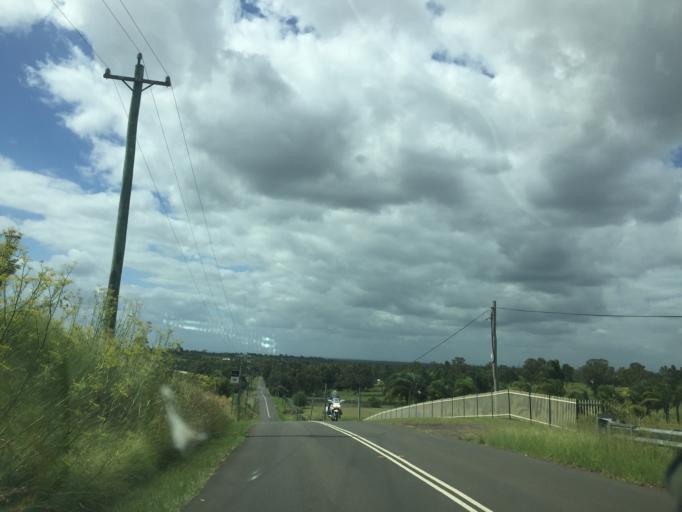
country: AU
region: New South Wales
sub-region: Penrith Municipality
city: Kingswood Park
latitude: -33.7925
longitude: 150.7376
